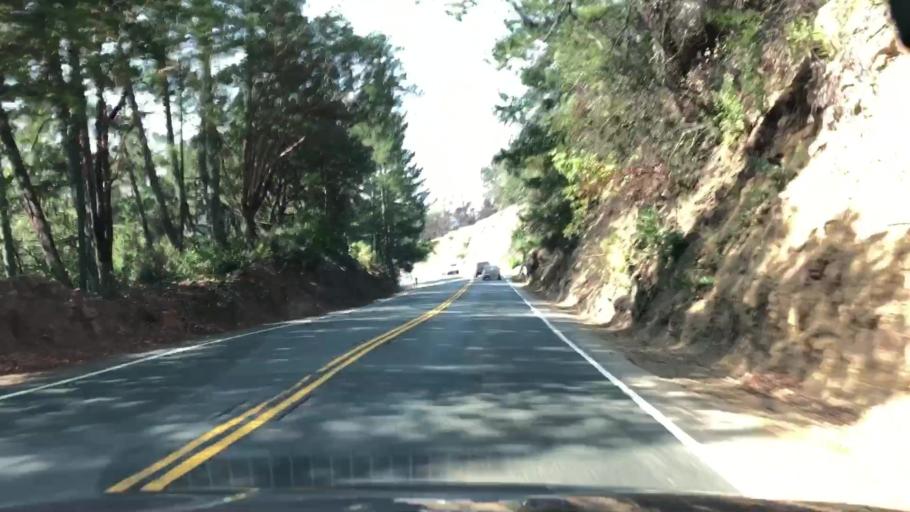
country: US
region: California
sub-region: Napa County
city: Calistoga
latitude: 38.6374
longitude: -122.6009
